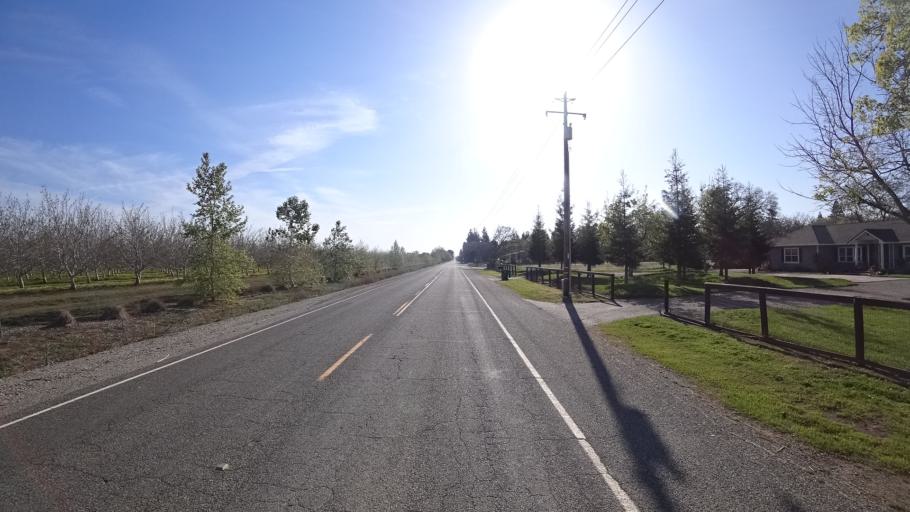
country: US
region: California
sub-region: Glenn County
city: Willows
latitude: 39.5388
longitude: -122.2088
